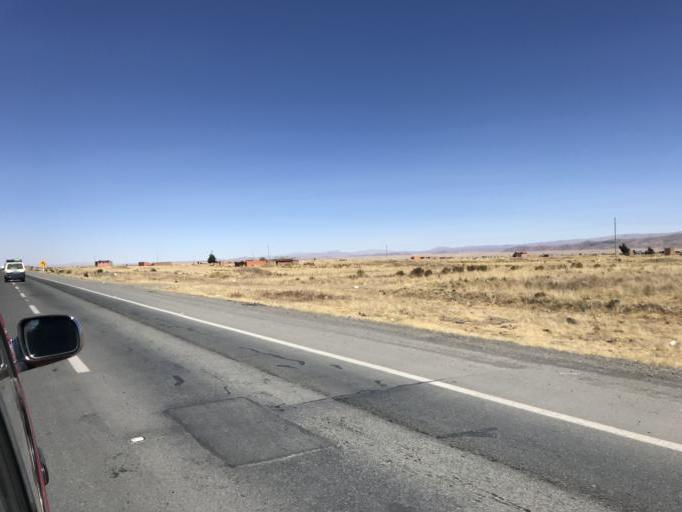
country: BO
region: La Paz
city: Batallas
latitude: -16.3567
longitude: -68.3982
